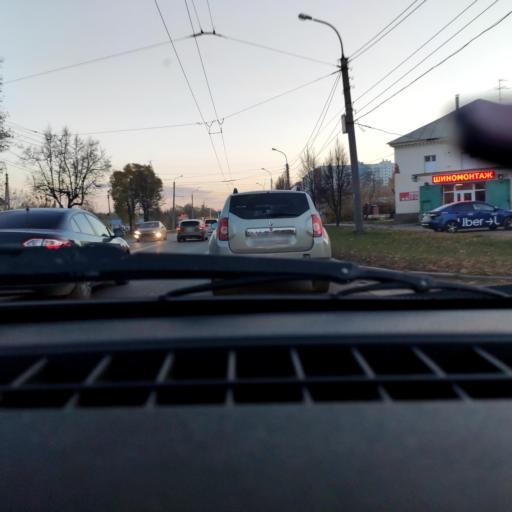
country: RU
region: Bashkortostan
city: Ufa
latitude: 54.7907
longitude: 56.1391
